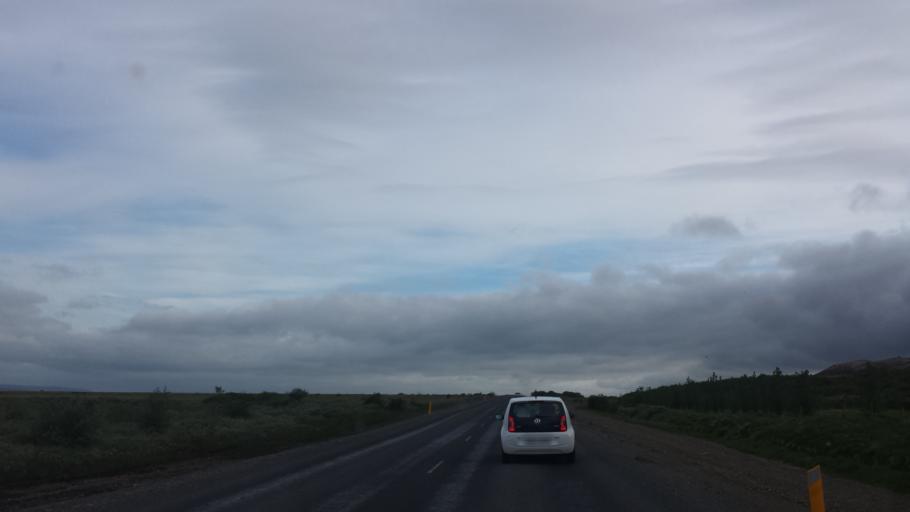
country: IS
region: South
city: Selfoss
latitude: 64.2913
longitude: -20.3370
